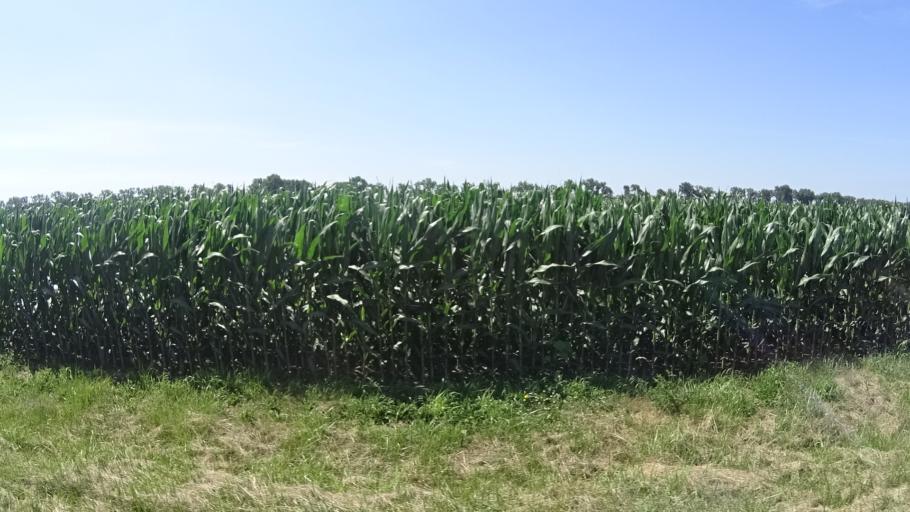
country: US
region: Ohio
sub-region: Erie County
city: Sandusky
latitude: 41.4300
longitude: -82.7876
